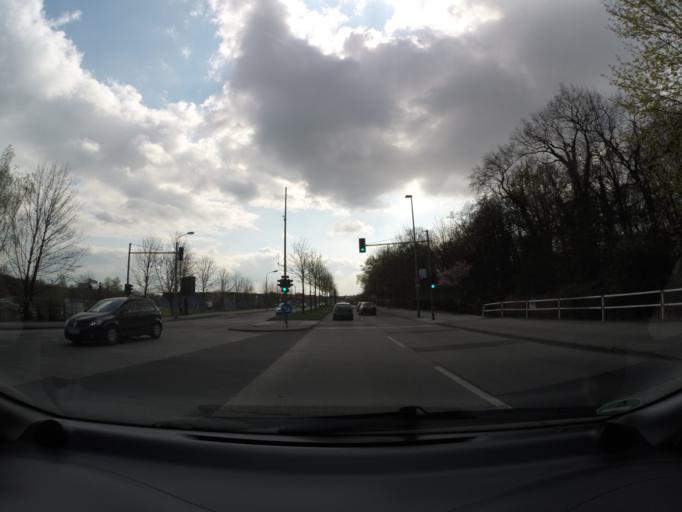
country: DE
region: Berlin
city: Hellersdorf
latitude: 52.5283
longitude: 13.6023
